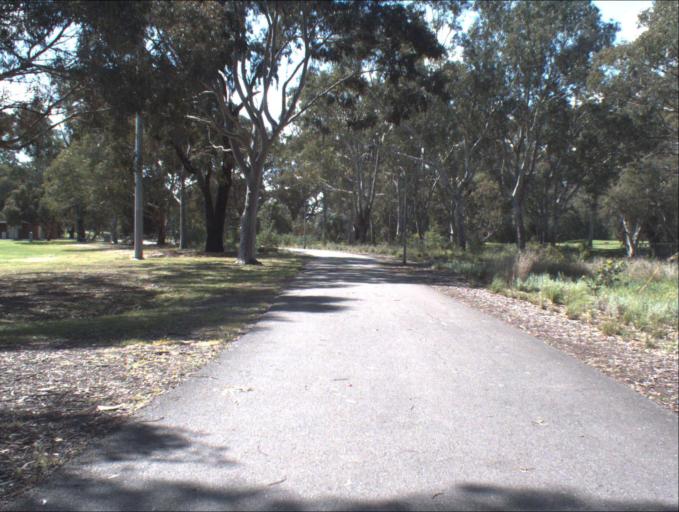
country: AU
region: South Australia
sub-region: Port Adelaide Enfield
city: Gilles Plains
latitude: -34.8437
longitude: 138.6658
